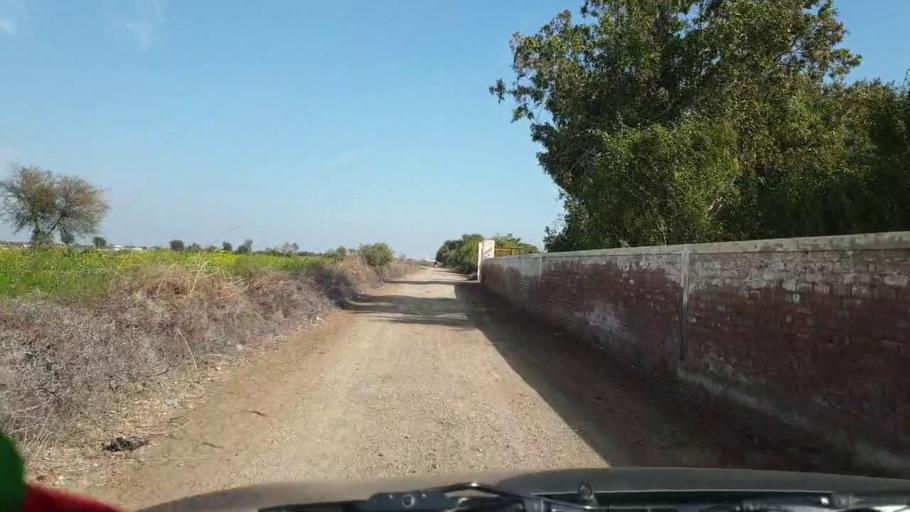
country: PK
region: Sindh
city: Sinjhoro
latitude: 26.0295
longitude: 68.8188
